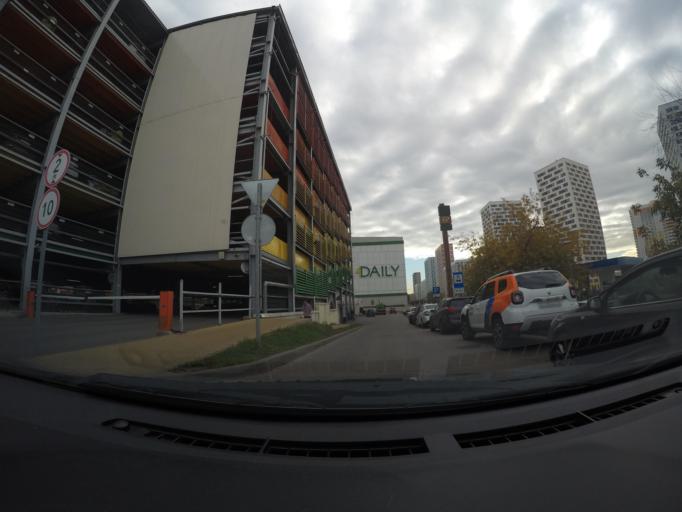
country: RU
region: Moskovskaya
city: Mytishchi
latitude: 55.9228
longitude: 37.7155
